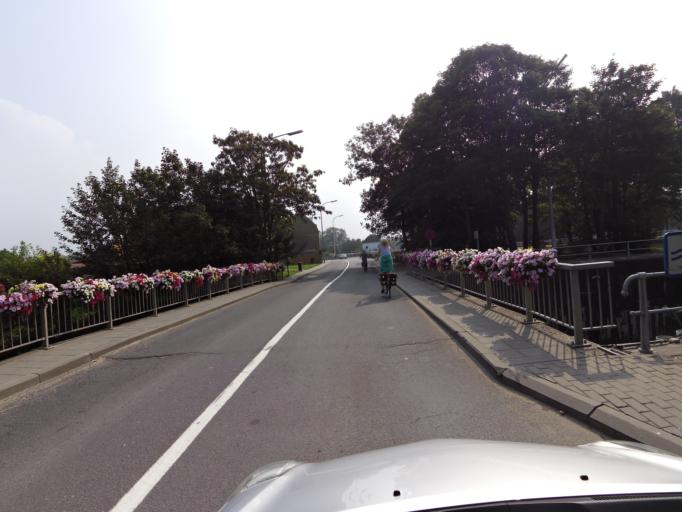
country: BE
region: Flanders
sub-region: Provincie West-Vlaanderen
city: Nieuwpoort
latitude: 51.1356
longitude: 2.7582
